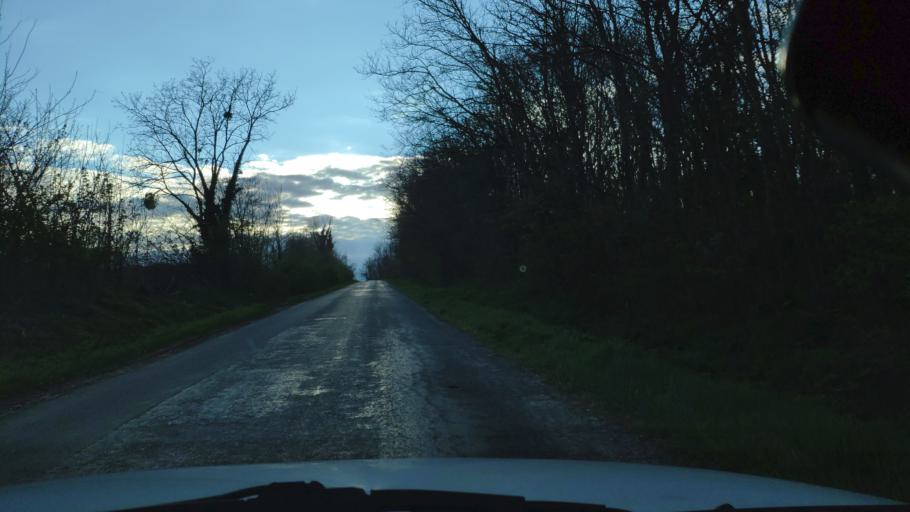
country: HU
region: Zala
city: Nagykanizsa
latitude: 46.4204
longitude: 17.1025
